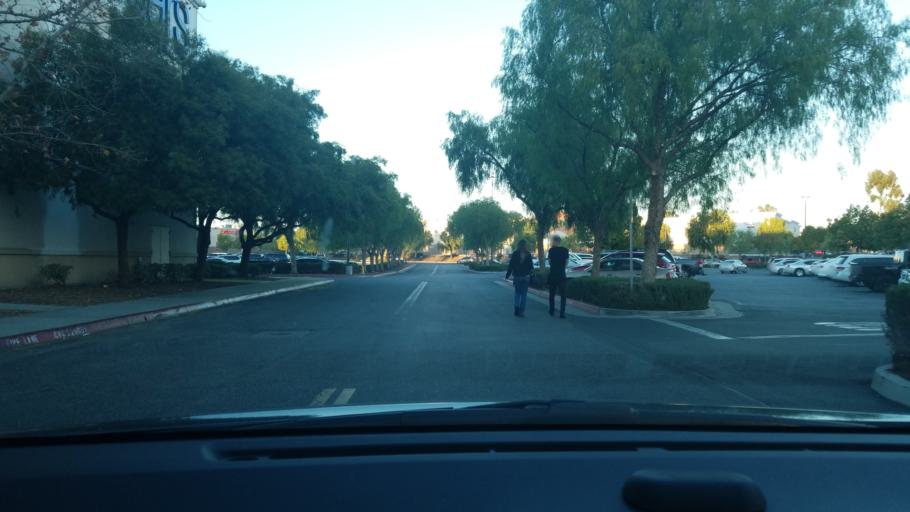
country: US
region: California
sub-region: Riverside County
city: Temecula
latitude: 33.5261
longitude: -117.1527
